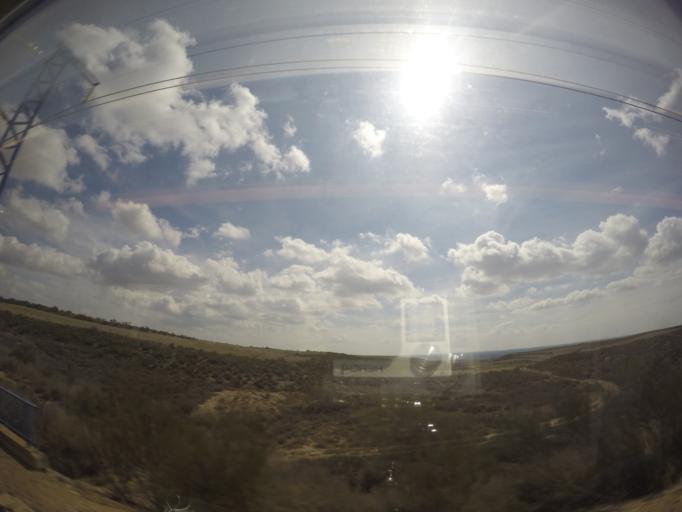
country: ES
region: Aragon
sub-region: Provincia de Huesca
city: Candasnos
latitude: 41.5728
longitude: 0.1091
